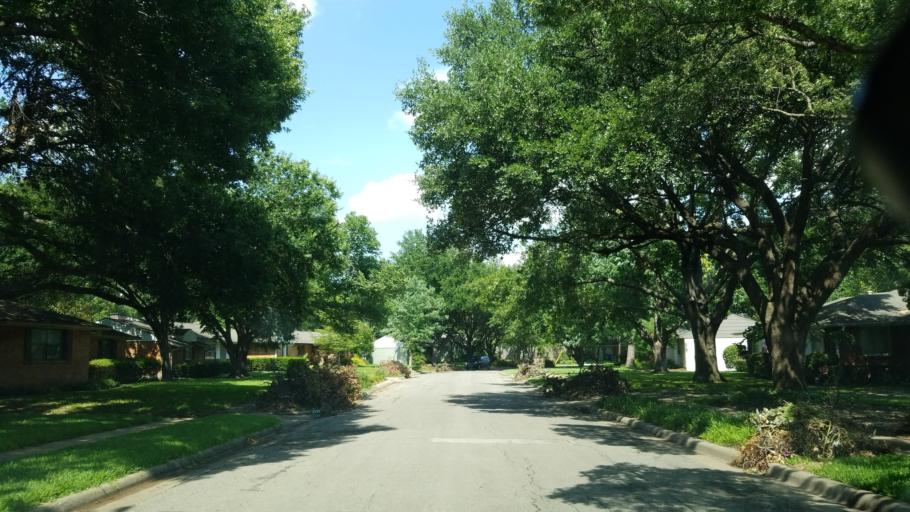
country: US
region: Texas
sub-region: Dallas County
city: Farmers Branch
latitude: 32.8868
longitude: -96.8606
